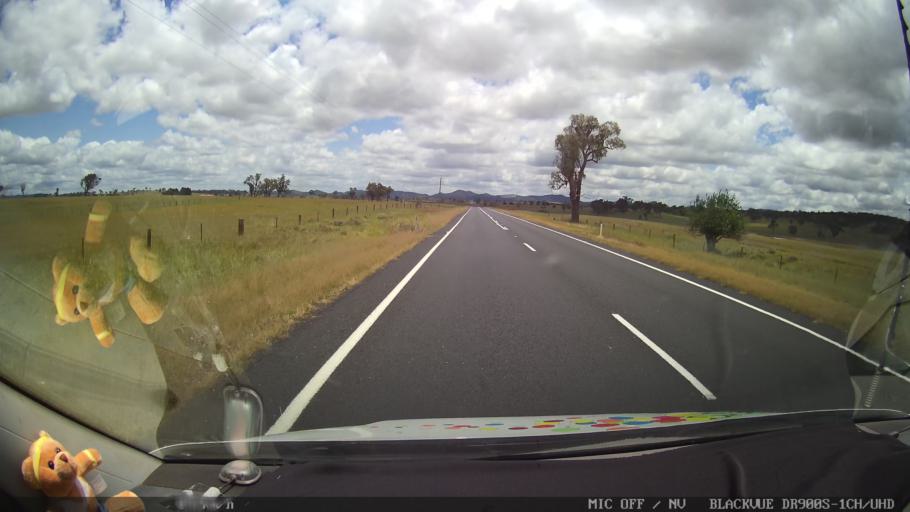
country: AU
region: New South Wales
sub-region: Glen Innes Severn
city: Glen Innes
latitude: -29.4245
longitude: 151.8590
